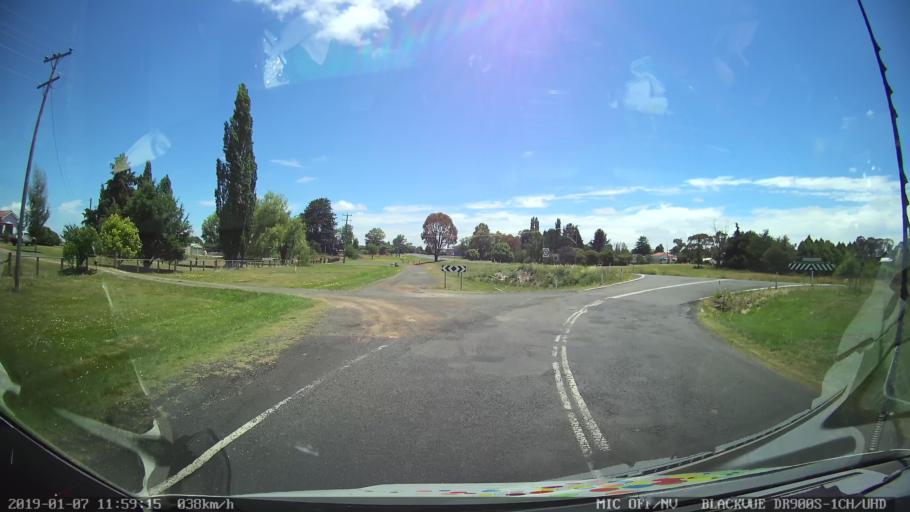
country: AU
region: New South Wales
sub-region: Guyra
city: Guyra
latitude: -30.2454
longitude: 151.6693
